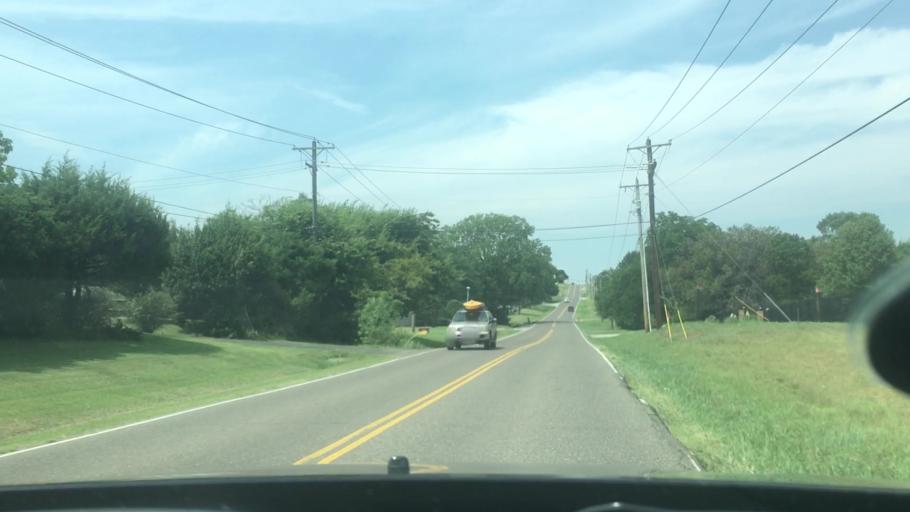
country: US
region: Oklahoma
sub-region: Pottawatomie County
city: Shawnee
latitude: 35.3617
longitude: -96.9025
